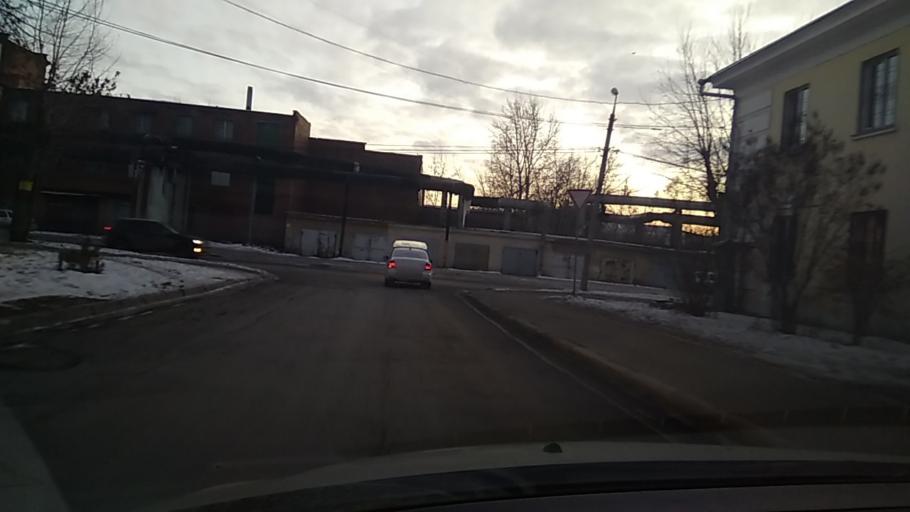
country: RU
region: Sverdlovsk
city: Istok
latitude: 56.7590
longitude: 60.7118
